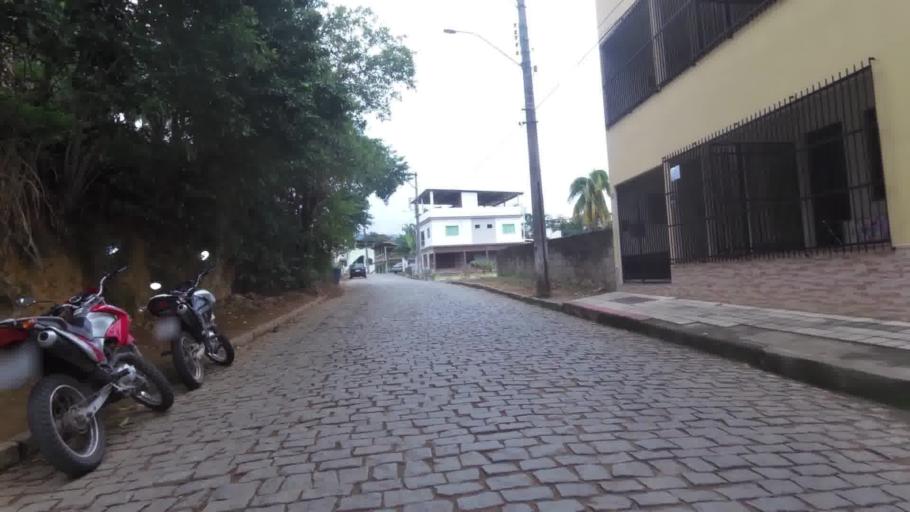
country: BR
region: Espirito Santo
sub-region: Iconha
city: Iconha
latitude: -20.7910
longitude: -40.8135
